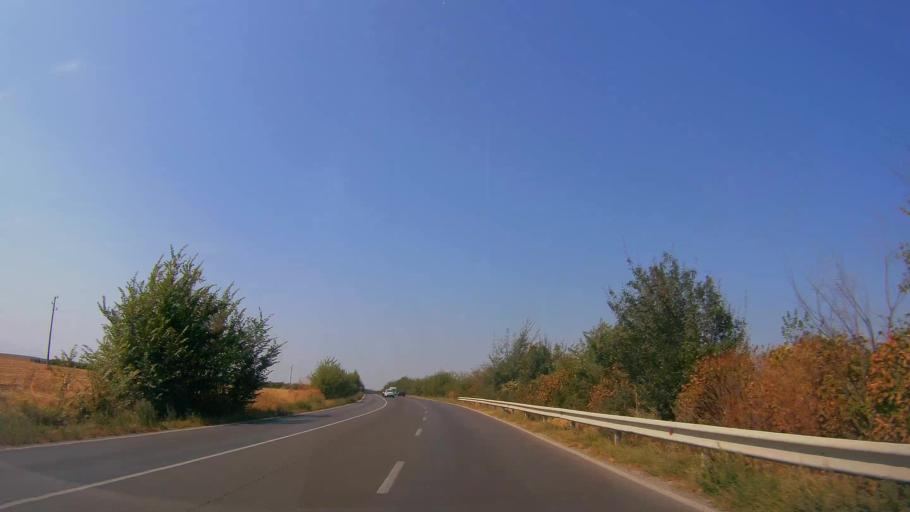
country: BG
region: Ruse
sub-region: Obshtina Vetovo
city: Senovo
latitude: 43.5640
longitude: 26.3398
